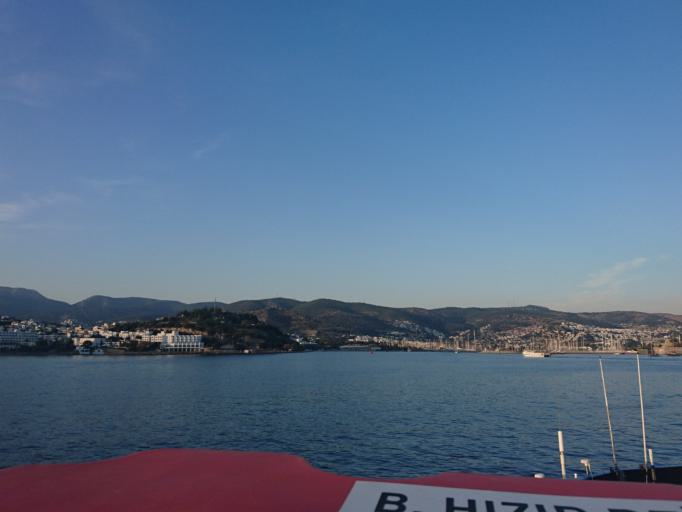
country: TR
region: Mugla
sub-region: Bodrum
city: Bodrum
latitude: 37.0225
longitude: 27.4211
